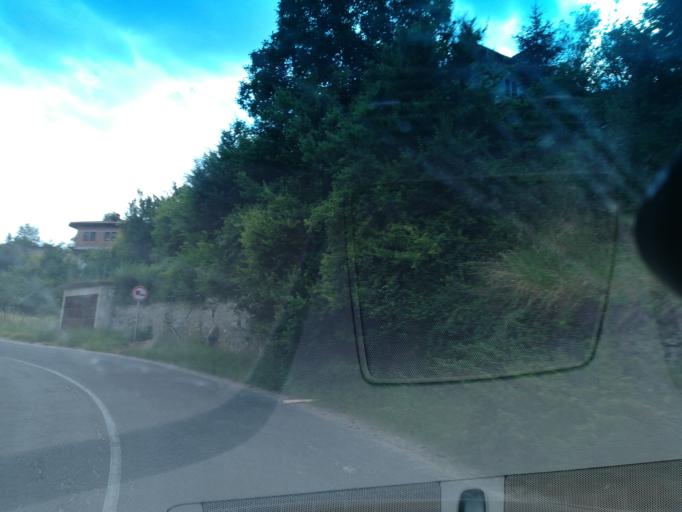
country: BG
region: Smolyan
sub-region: Obshtina Smolyan
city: Smolyan
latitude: 41.6537
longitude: 24.7715
